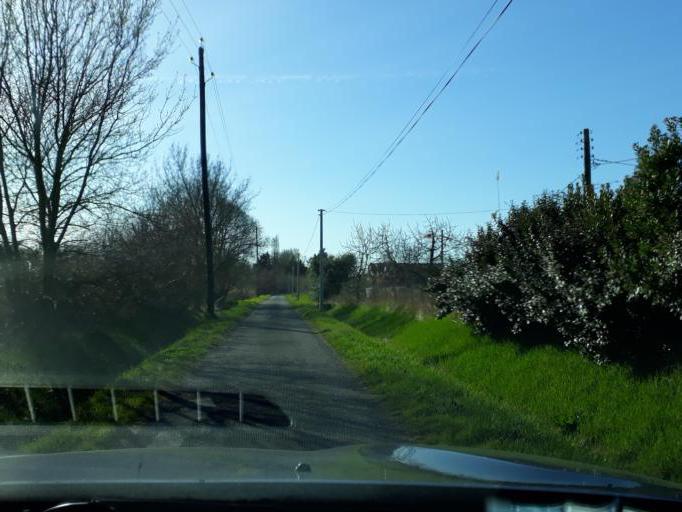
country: FR
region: Languedoc-Roussillon
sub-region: Departement de l'Herault
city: Agde
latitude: 43.3162
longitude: 3.4516
